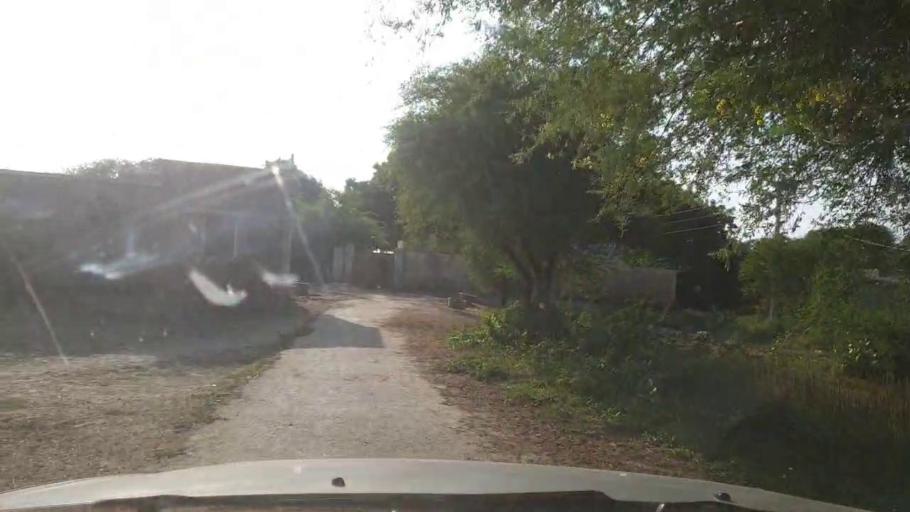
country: PK
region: Sindh
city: Tando Ghulam Ali
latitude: 25.1173
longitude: 68.9346
